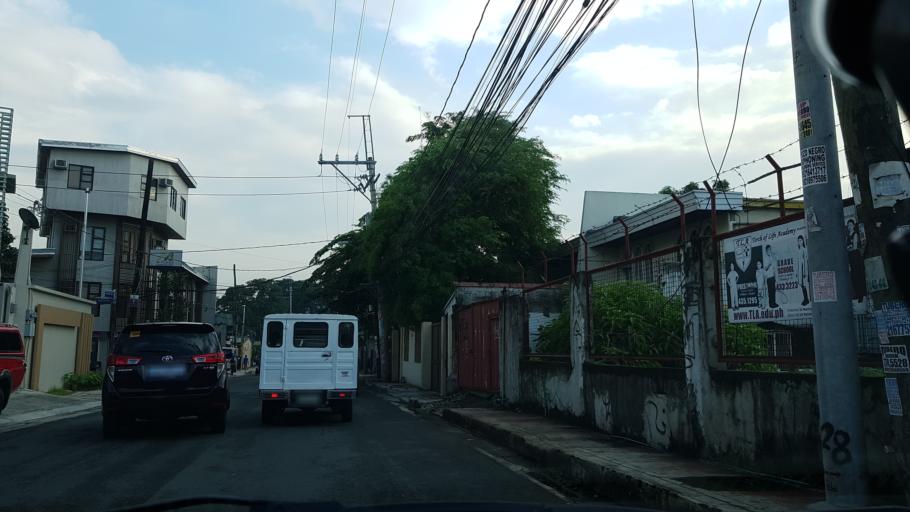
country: PH
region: Metro Manila
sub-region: Quezon City
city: Quezon City
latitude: 14.6383
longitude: 121.0581
